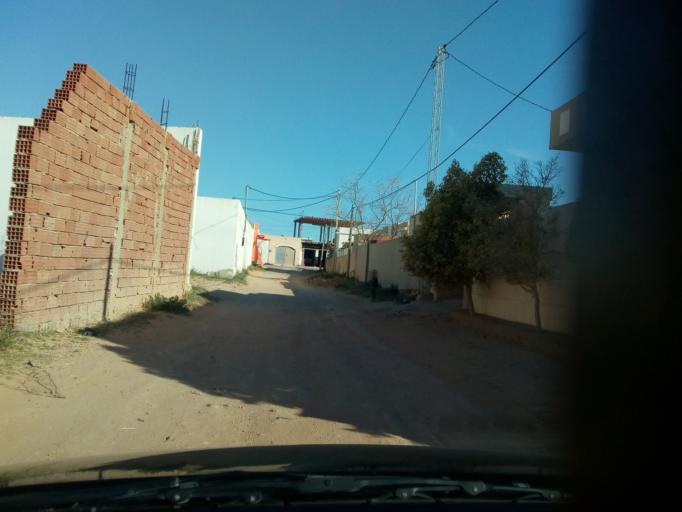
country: TN
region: Safaqis
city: Sfax
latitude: 34.7281
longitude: 10.6254
